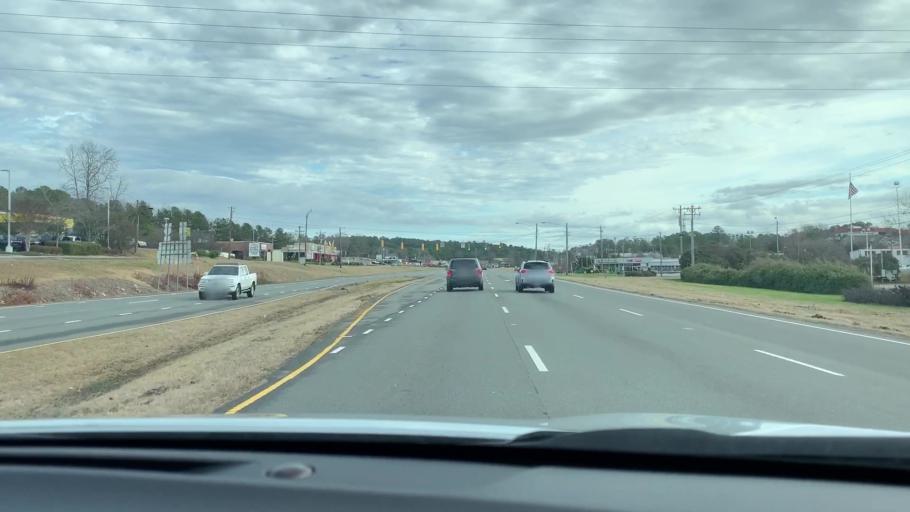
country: US
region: North Carolina
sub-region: Durham County
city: Durham
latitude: 35.9698
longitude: -78.9567
